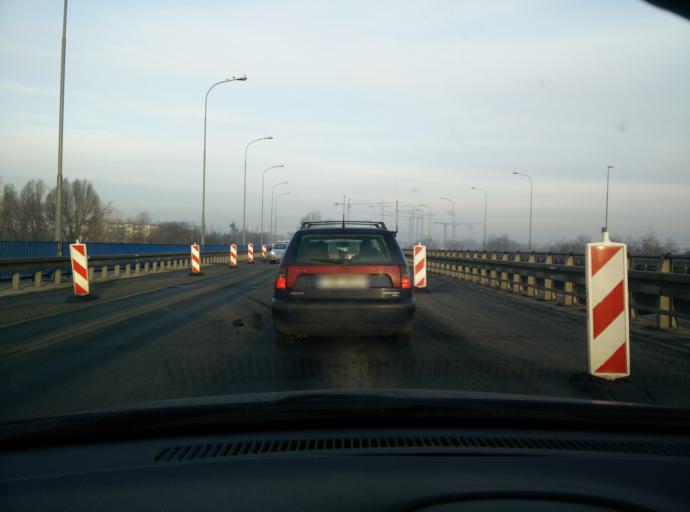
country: PL
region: Greater Poland Voivodeship
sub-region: Poznan
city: Poznan
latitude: 52.3906
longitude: 16.9642
